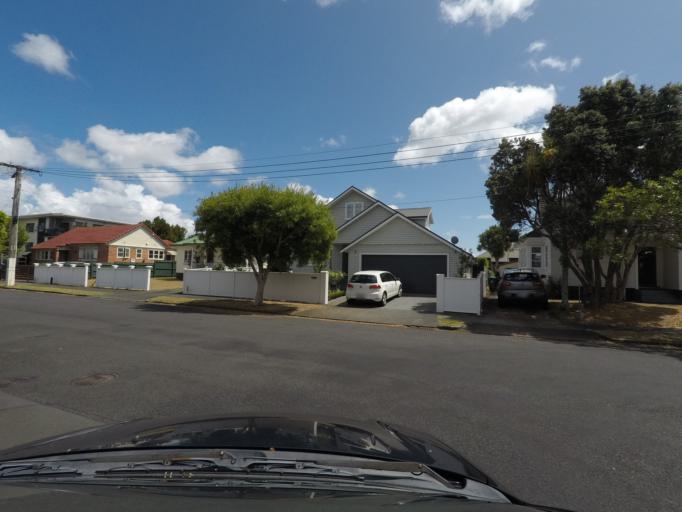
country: NZ
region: Auckland
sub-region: Auckland
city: Rosebank
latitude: -36.8634
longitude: 174.7013
